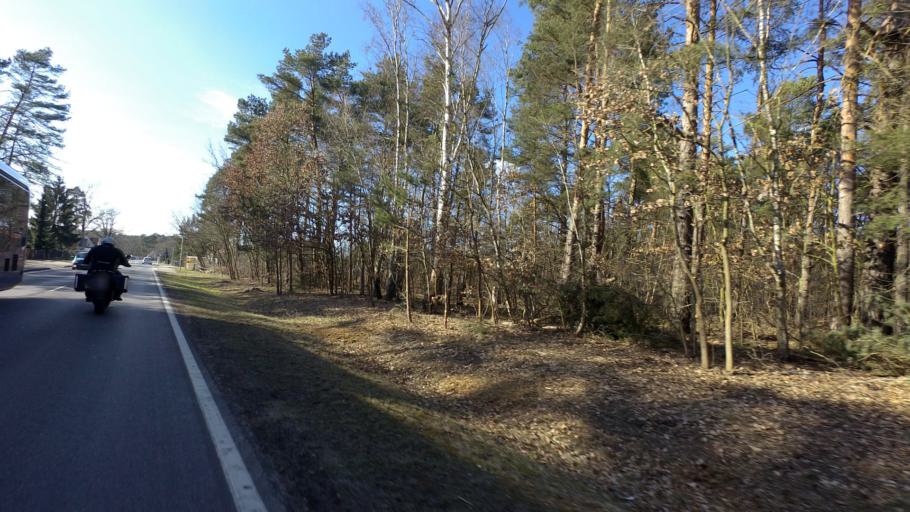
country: DE
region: Brandenburg
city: Oranienburg
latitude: 52.7621
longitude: 13.3329
